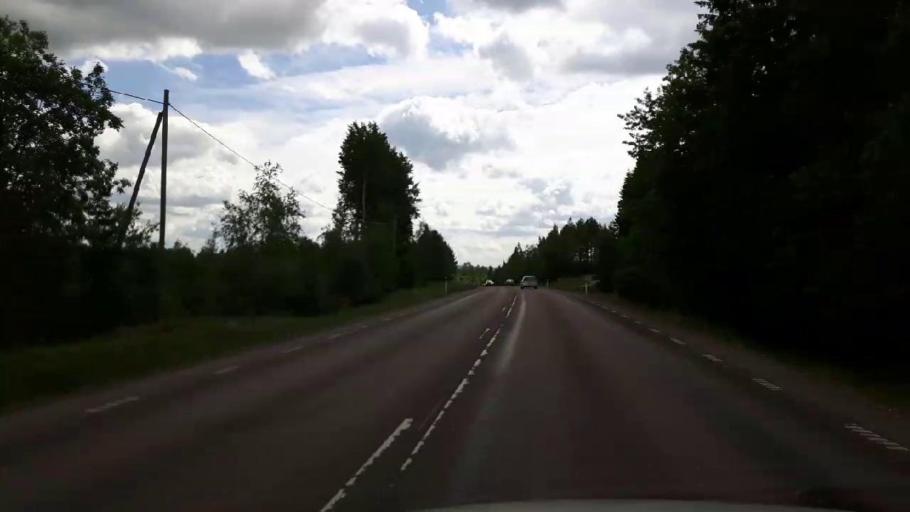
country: SE
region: Dalarna
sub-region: Saters Kommun
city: Saeter
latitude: 60.4657
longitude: 15.7986
